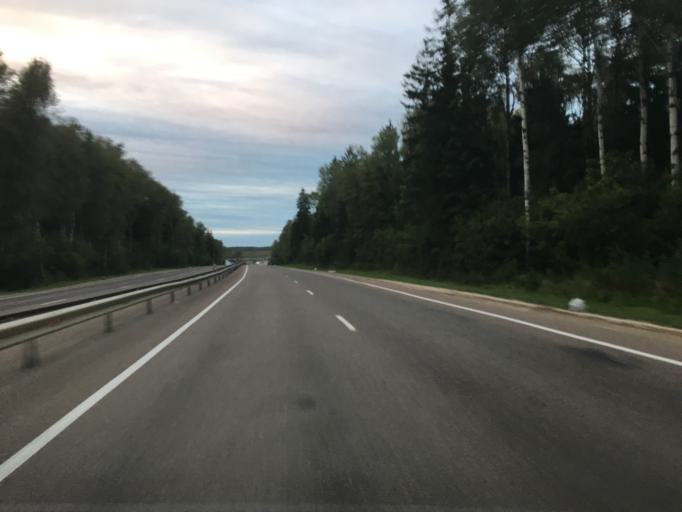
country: RU
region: Kaluga
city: Kaluga
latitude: 54.6415
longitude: 36.2990
